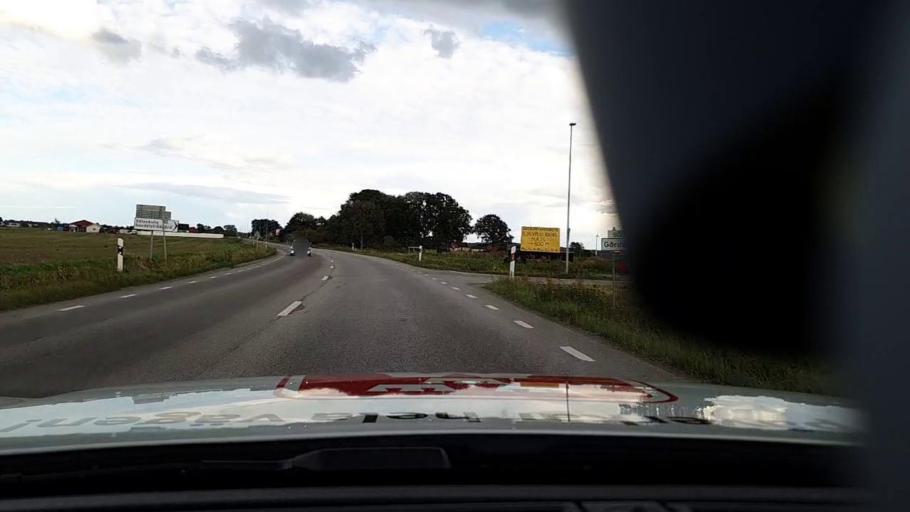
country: SE
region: Blekinge
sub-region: Solvesborgs Kommun
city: Soelvesborg
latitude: 56.0548
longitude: 14.6384
